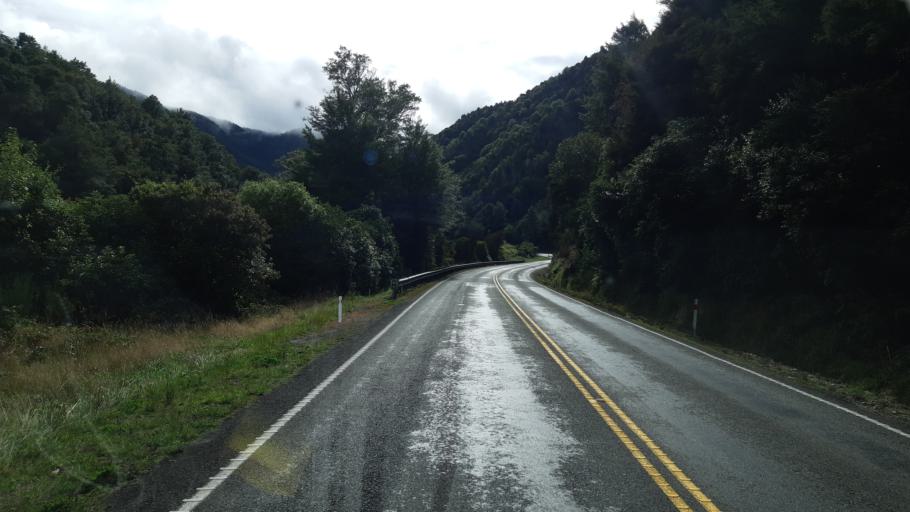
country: NZ
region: West Coast
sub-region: Buller District
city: Westport
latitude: -41.7751
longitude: 172.2232
